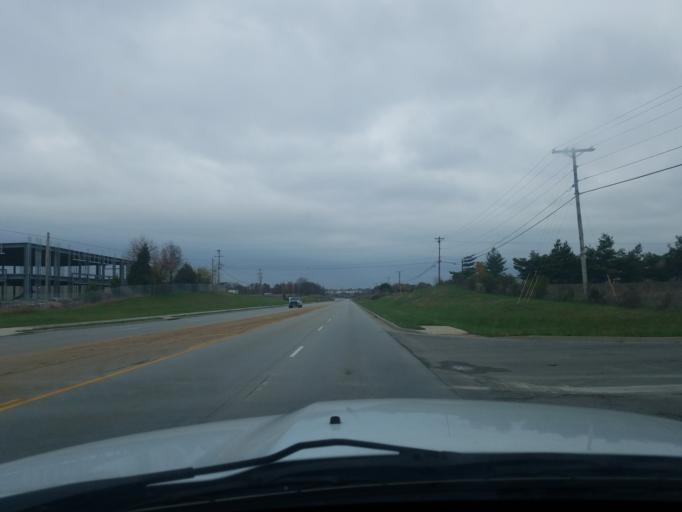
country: US
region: Kentucky
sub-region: Nelson County
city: Bardstown
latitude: 37.8031
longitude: -85.4323
